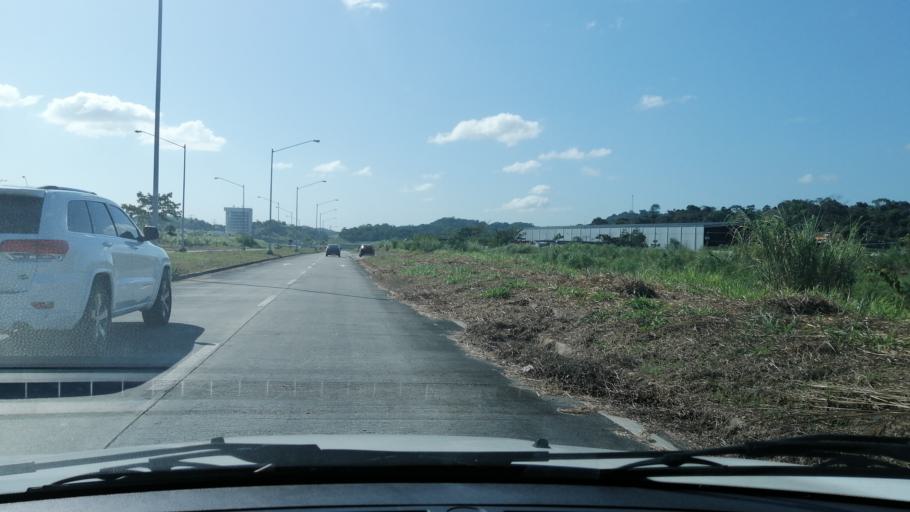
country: PA
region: Panama
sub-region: Distrito de Panama
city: Paraiso
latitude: 9.0308
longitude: -79.5823
